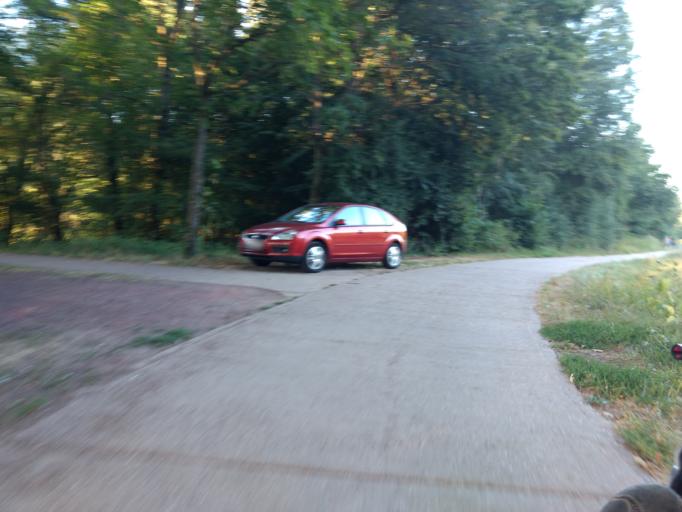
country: DE
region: Saarland
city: Rehlingen-Siersburg
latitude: 49.3641
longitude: 6.6447
